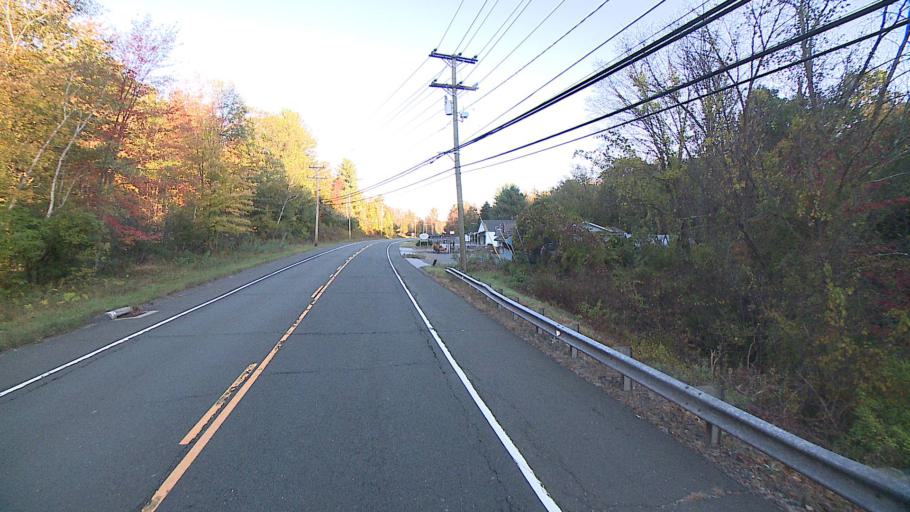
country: US
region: Connecticut
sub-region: Litchfield County
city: New Hartford Center
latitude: 41.9030
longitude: -72.9958
